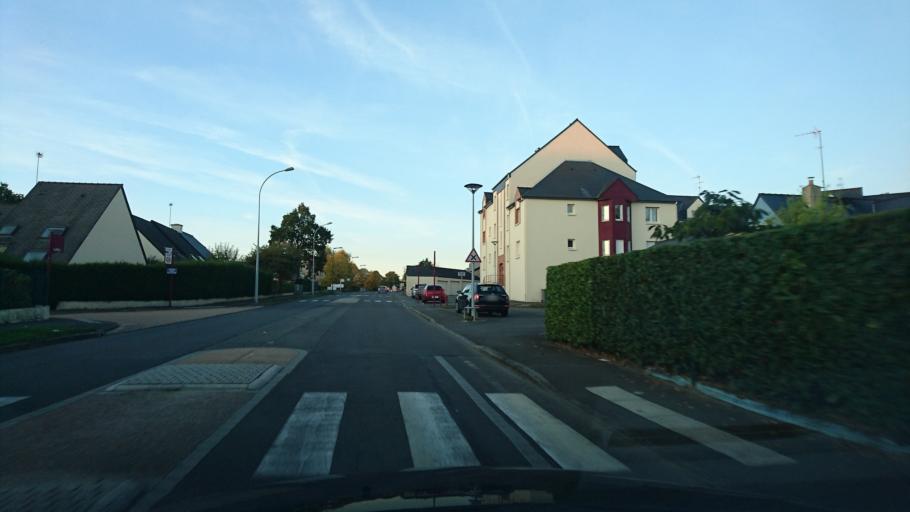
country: FR
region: Brittany
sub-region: Departement d'Ille-et-Vilaine
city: Bruz
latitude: 48.0230
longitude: -1.7527
